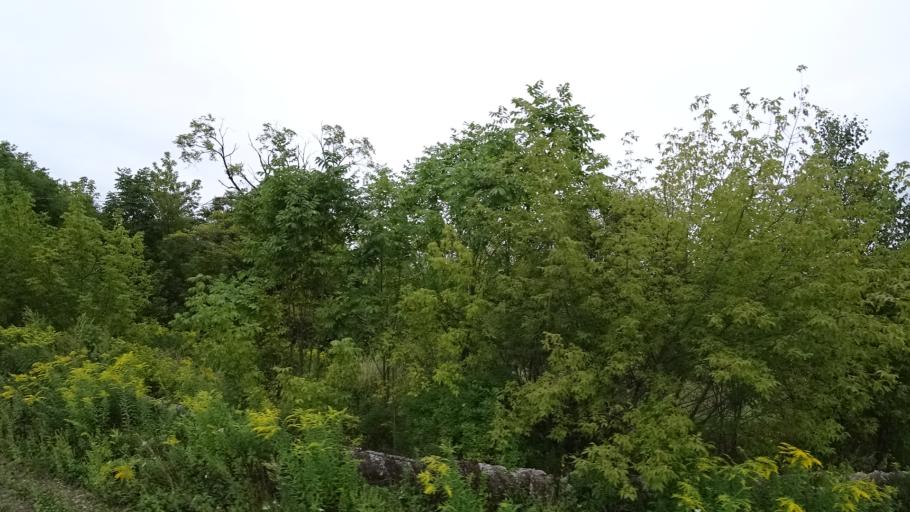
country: RU
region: Primorskiy
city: Rettikhovka
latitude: 44.1587
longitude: 132.7447
